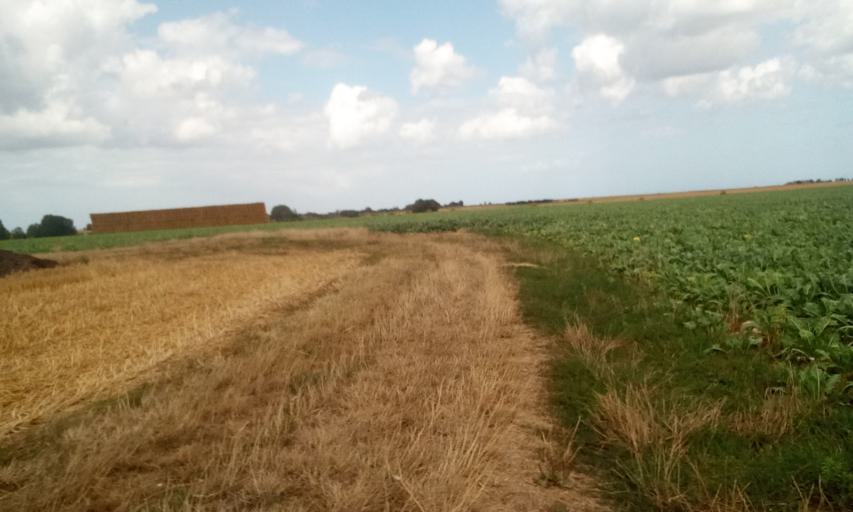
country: FR
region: Lower Normandy
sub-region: Departement du Calvados
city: Ver-sur-Mer
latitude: 49.3121
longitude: -0.5408
